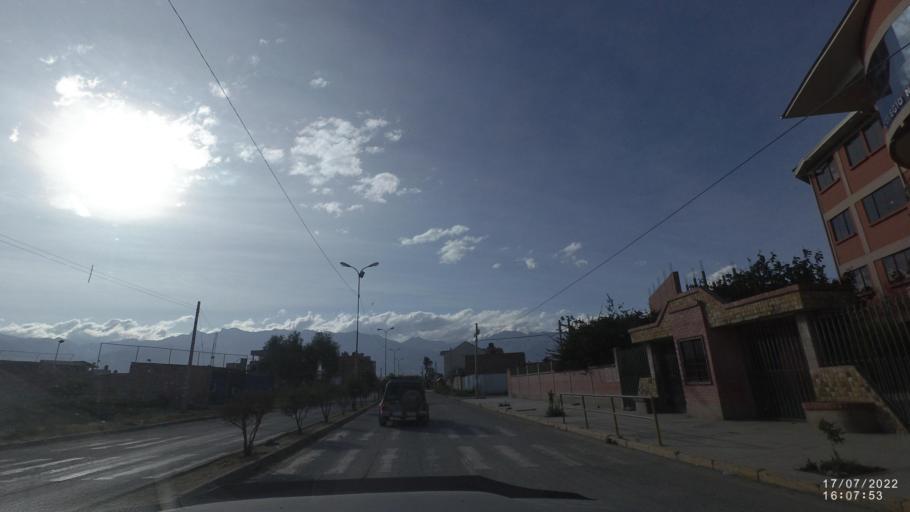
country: BO
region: Cochabamba
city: Sipe Sipe
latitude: -17.4116
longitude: -66.2724
